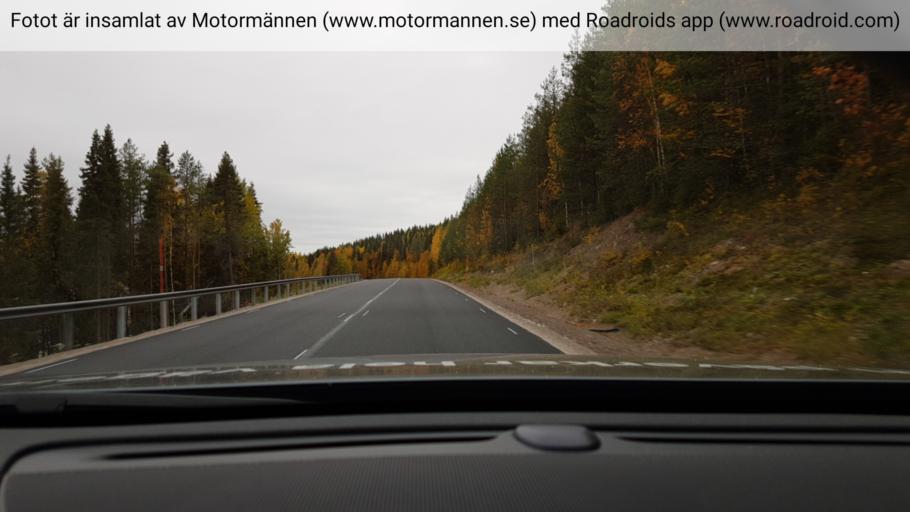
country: SE
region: Norrbotten
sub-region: Overkalix Kommun
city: OEverkalix
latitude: 66.4808
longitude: 22.7859
